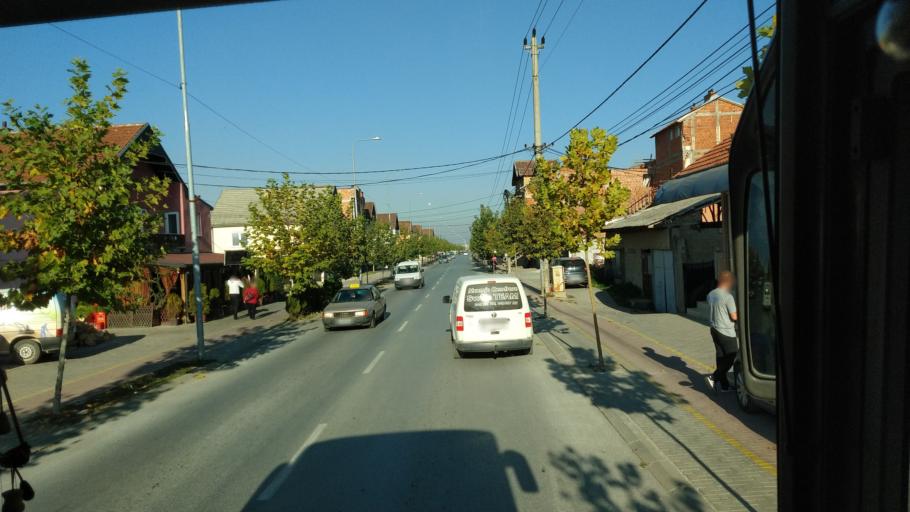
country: XK
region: Ferizaj
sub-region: Komuna e Shtimes
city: Shtime
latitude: 42.4352
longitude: 21.0442
